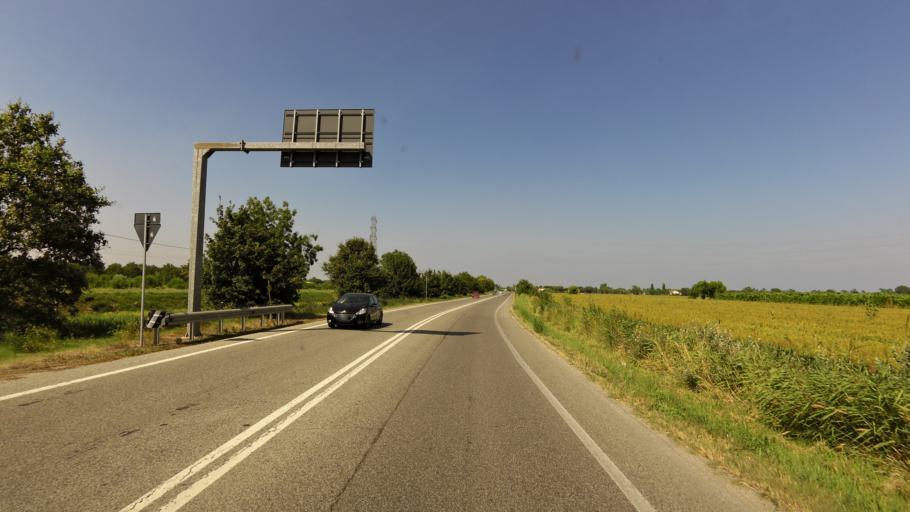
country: IT
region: Emilia-Romagna
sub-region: Provincia di Ravenna
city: Porto Fuori
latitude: 44.4110
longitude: 12.2309
